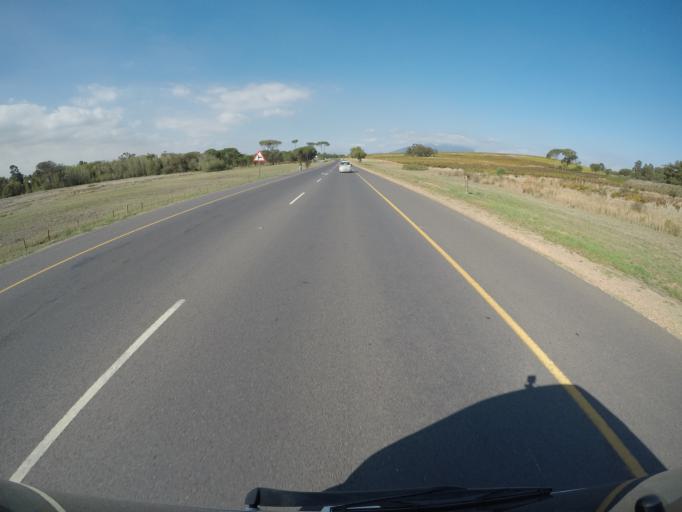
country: ZA
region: Western Cape
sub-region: City of Cape Town
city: Kraaifontein
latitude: -33.8811
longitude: 18.7610
